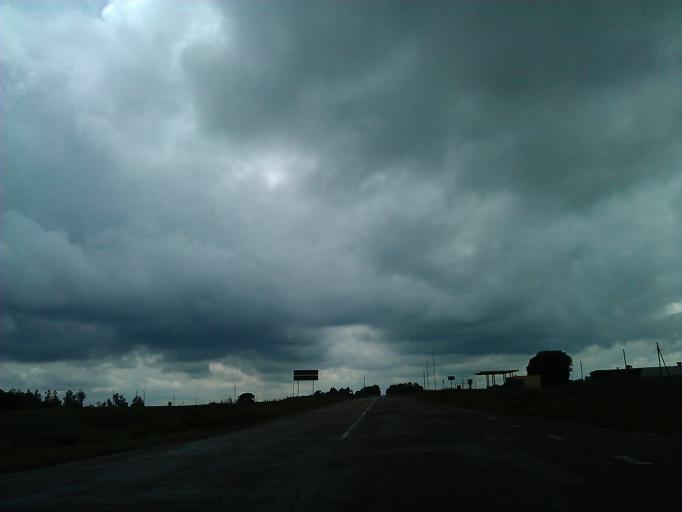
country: LV
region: Aizpute
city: Aizpute
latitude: 56.8399
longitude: 21.7659
